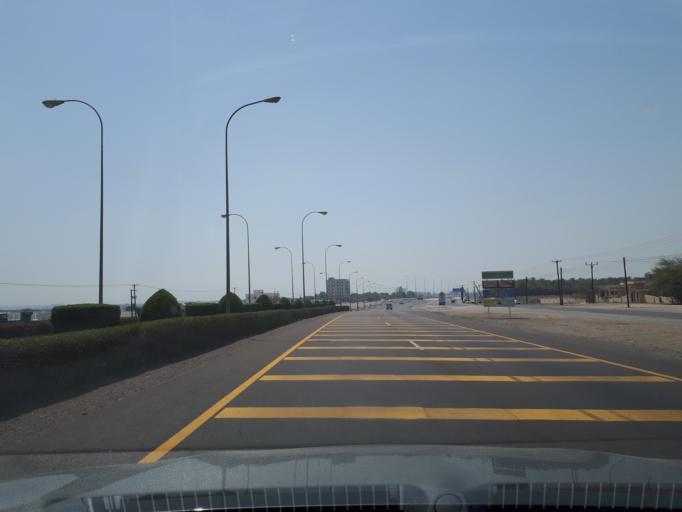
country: OM
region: Al Batinah
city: Al Sohar
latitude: 24.4129
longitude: 56.6343
